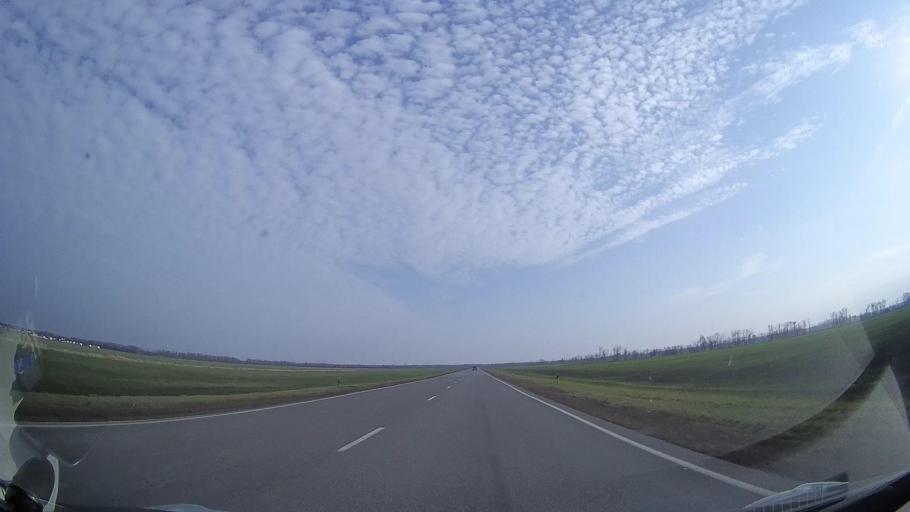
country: RU
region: Rostov
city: Tselina
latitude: 46.5137
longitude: 41.0467
